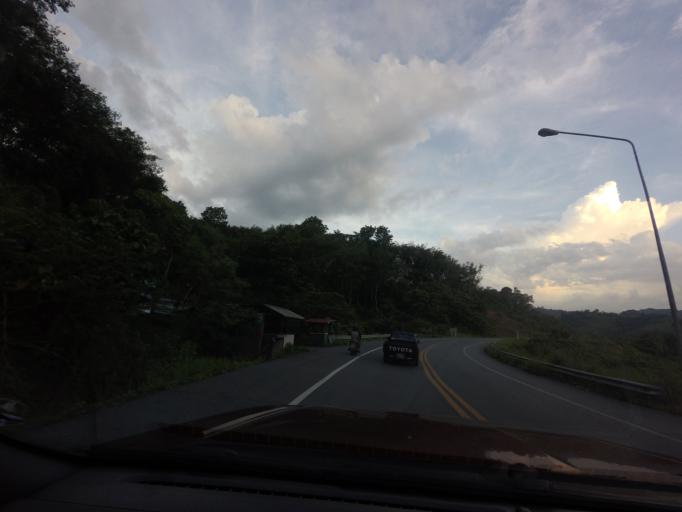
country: TH
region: Yala
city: Than To
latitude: 6.0606
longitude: 101.1946
